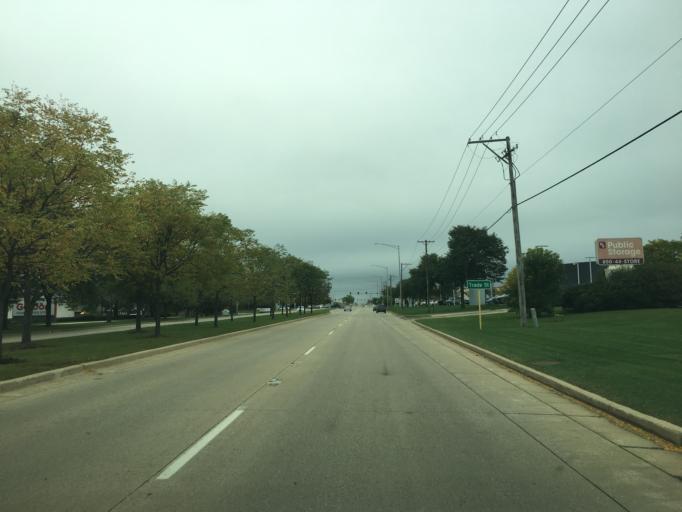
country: US
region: Illinois
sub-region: DuPage County
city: Naperville
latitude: 41.7512
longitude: -88.2126
